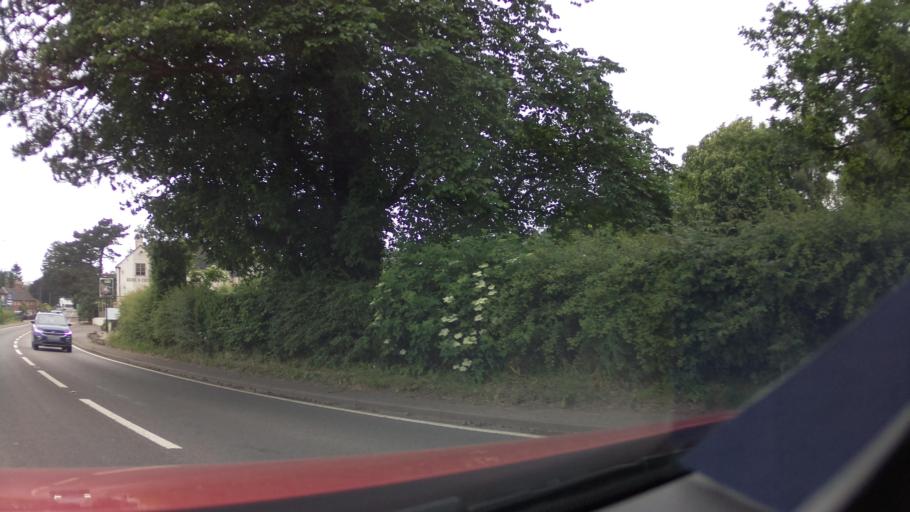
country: GB
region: England
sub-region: Derbyshire
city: Yeldersley
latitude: 52.9668
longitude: -1.6155
